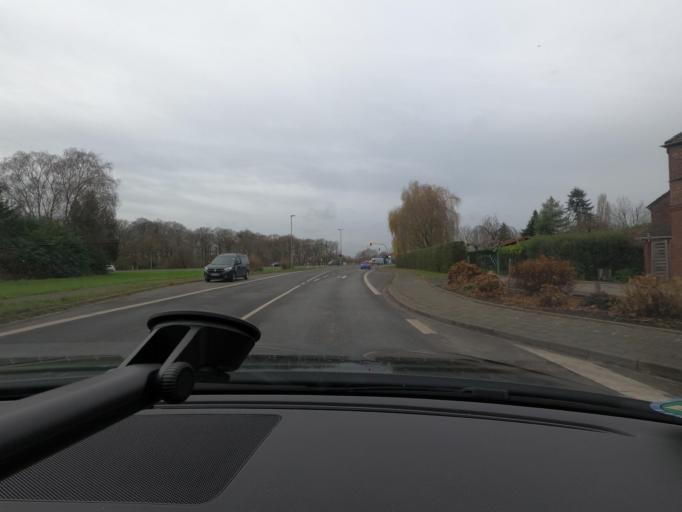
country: DE
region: North Rhine-Westphalia
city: Tonisvorst
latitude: 51.3503
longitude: 6.4643
